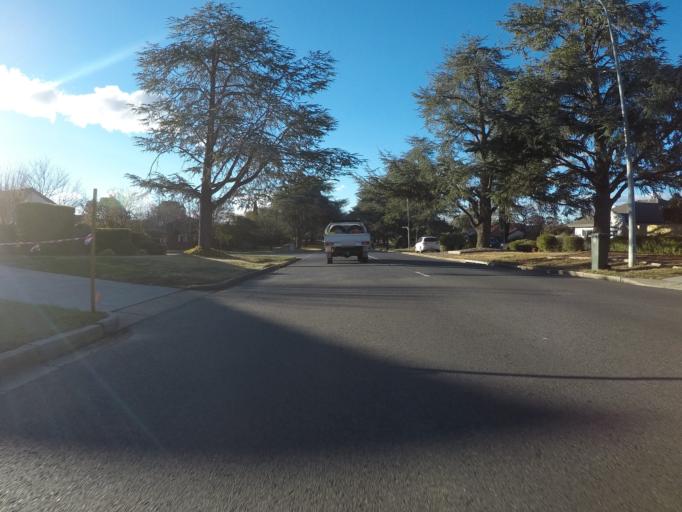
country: AU
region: Australian Capital Territory
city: Forrest
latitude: -35.3117
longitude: 149.0982
